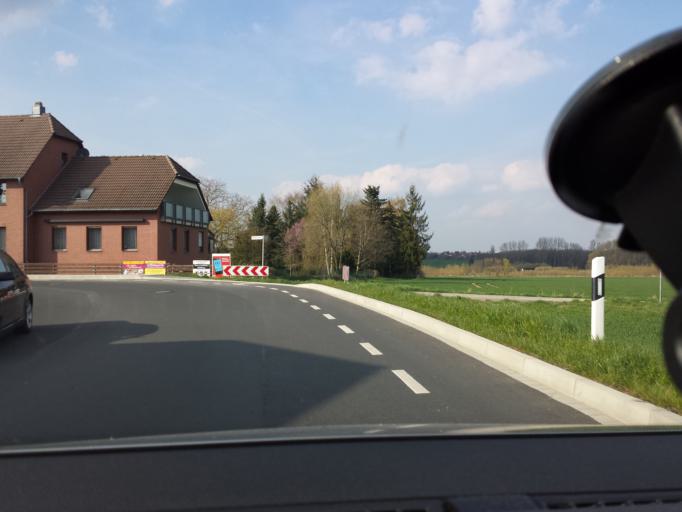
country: DE
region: Lower Saxony
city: Klein Schwulper
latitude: 52.2694
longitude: 10.4478
